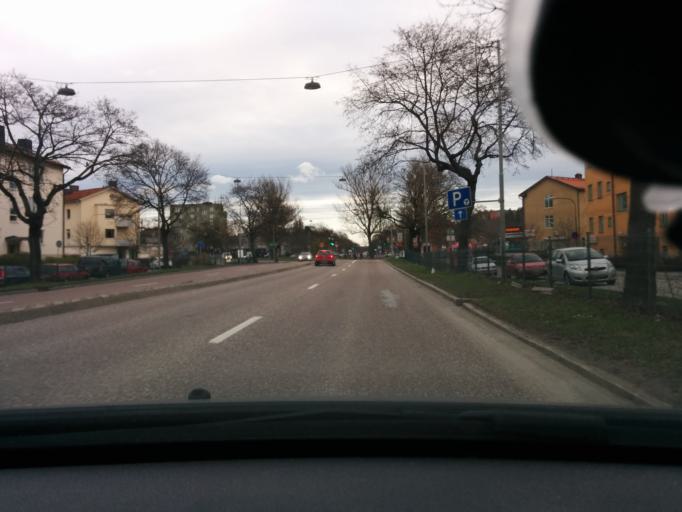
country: SE
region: Stockholm
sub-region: Stockholms Kommun
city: Bromma
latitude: 59.3402
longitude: 17.9367
